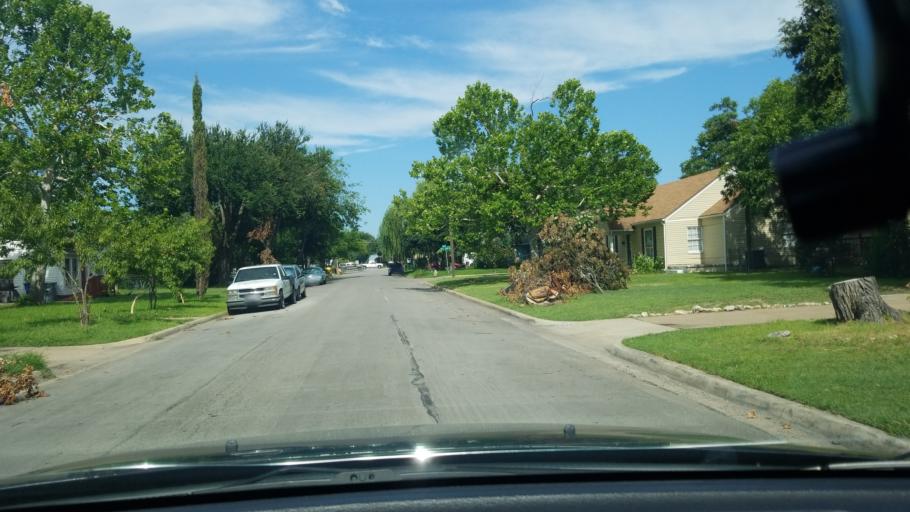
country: US
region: Texas
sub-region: Dallas County
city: Balch Springs
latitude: 32.7711
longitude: -96.6808
